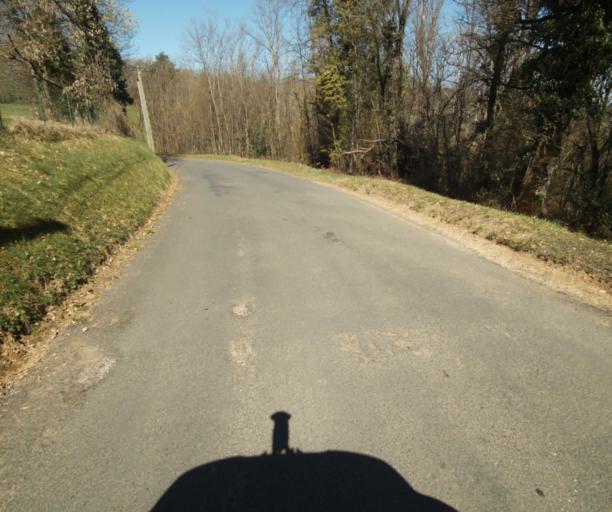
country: FR
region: Limousin
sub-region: Departement de la Correze
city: Naves
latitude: 45.3061
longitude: 1.7200
